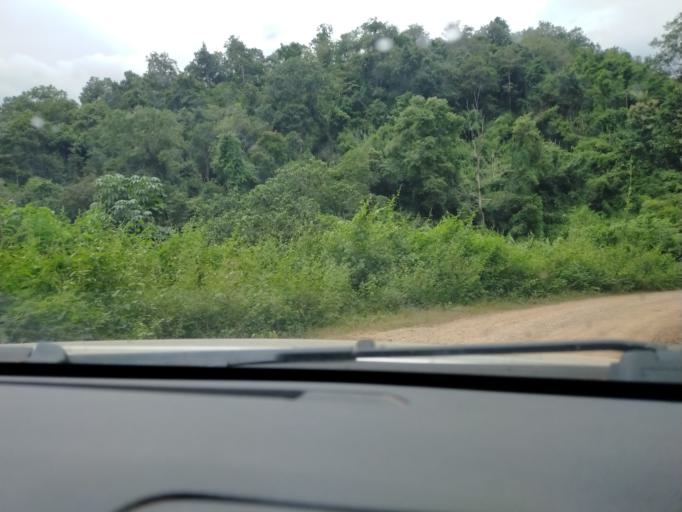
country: TH
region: Nan
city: Chaloem Phra Kiat
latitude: 19.8111
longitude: 101.3627
